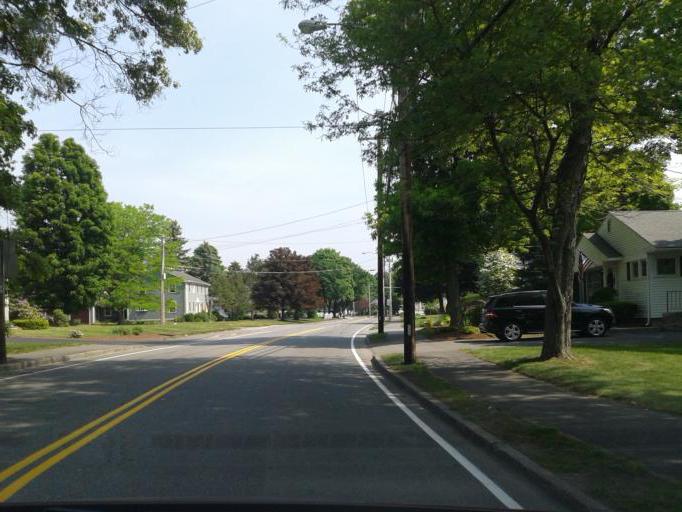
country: US
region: Massachusetts
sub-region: Worcester County
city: Westborough
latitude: 42.2614
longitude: -71.6102
